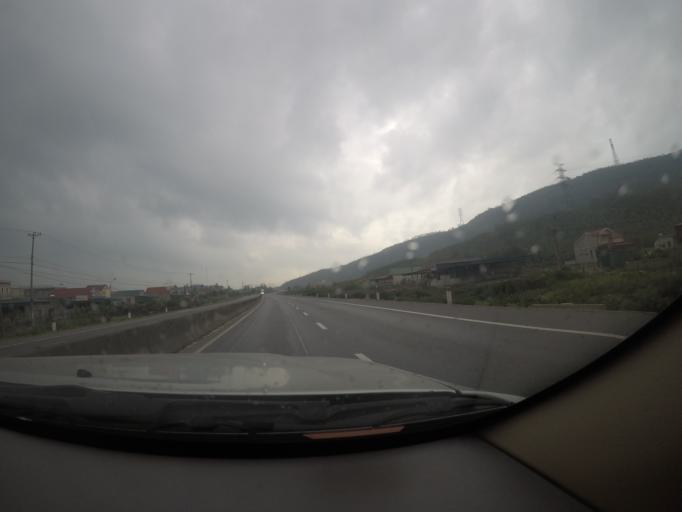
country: VN
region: Ha Tinh
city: Ky Anh
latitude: 17.9902
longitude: 106.4734
